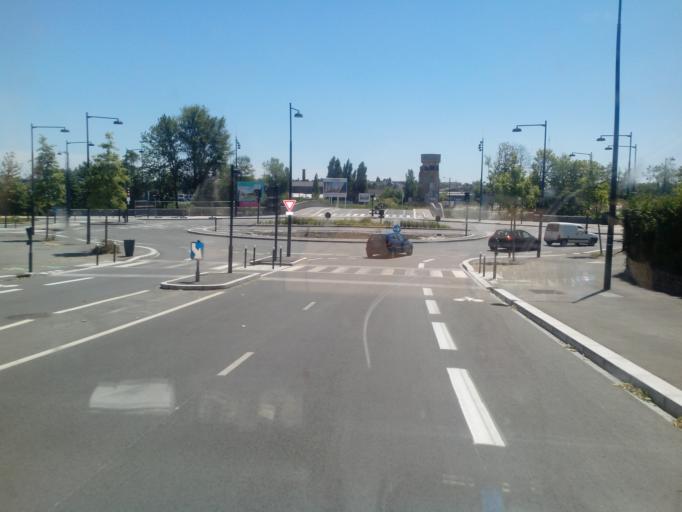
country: FR
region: Brittany
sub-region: Departement d'Ille-et-Vilaine
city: Rennes
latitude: 48.1122
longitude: -1.6466
